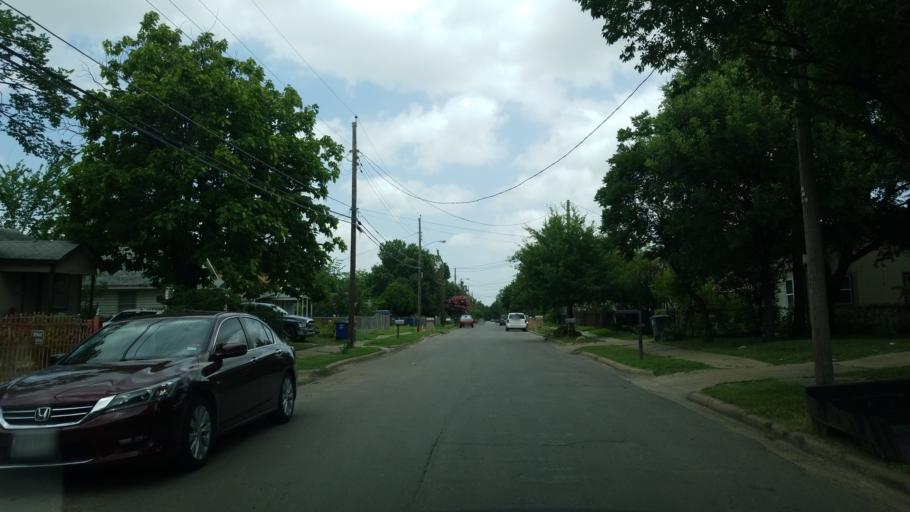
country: US
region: Texas
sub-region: Dallas County
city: Cockrell Hill
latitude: 32.7856
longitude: -96.9035
